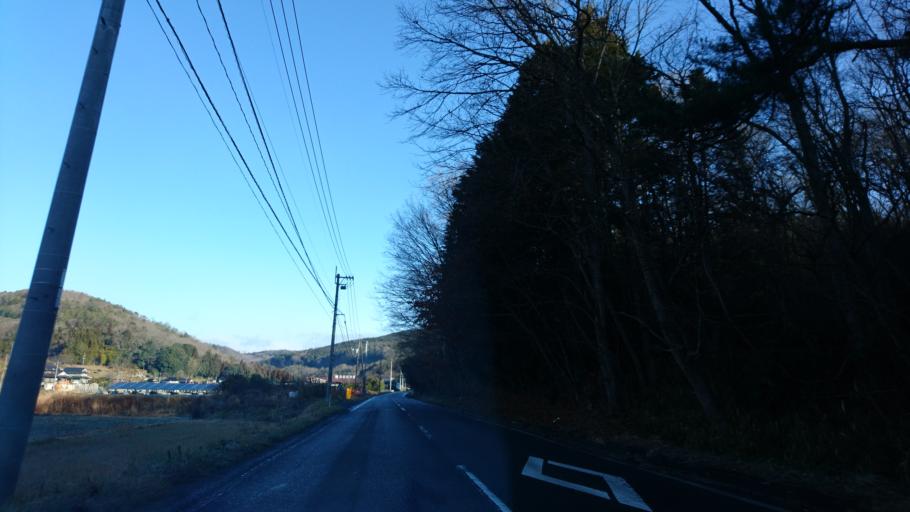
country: JP
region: Okayama
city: Takahashi
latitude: 34.8108
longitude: 133.6731
